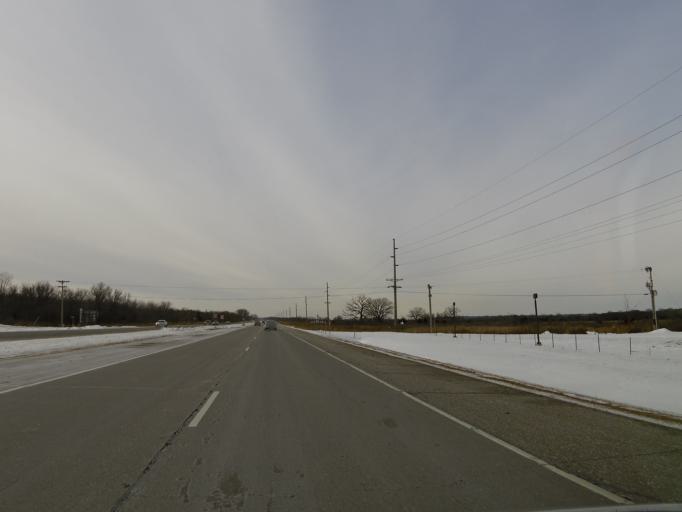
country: US
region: Minnesota
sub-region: Scott County
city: Jordan
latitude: 44.6538
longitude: -93.6846
